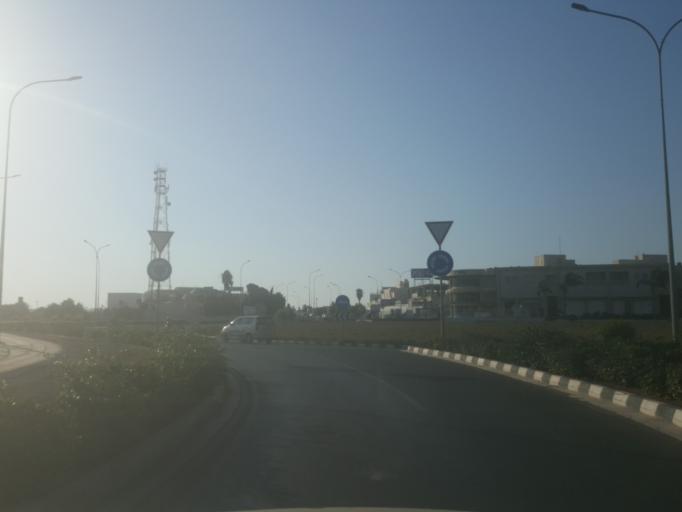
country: CY
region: Ammochostos
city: Paralimni
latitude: 35.0523
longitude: 33.9749
